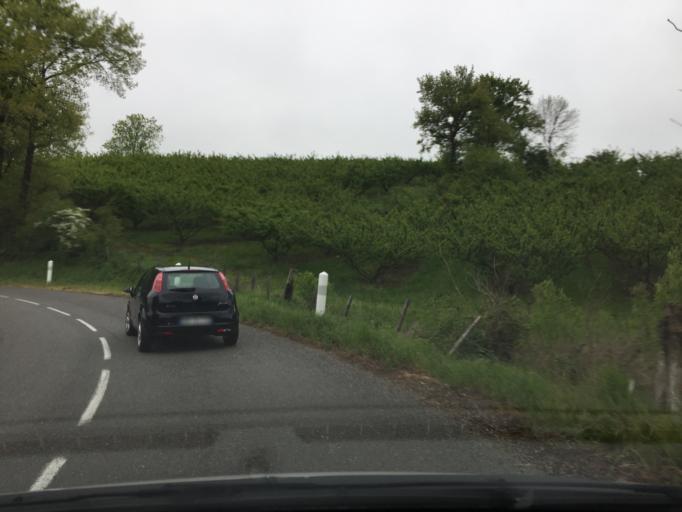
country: FR
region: Rhone-Alpes
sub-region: Departement du Rhone
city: Mornant
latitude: 45.6018
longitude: 4.6666
